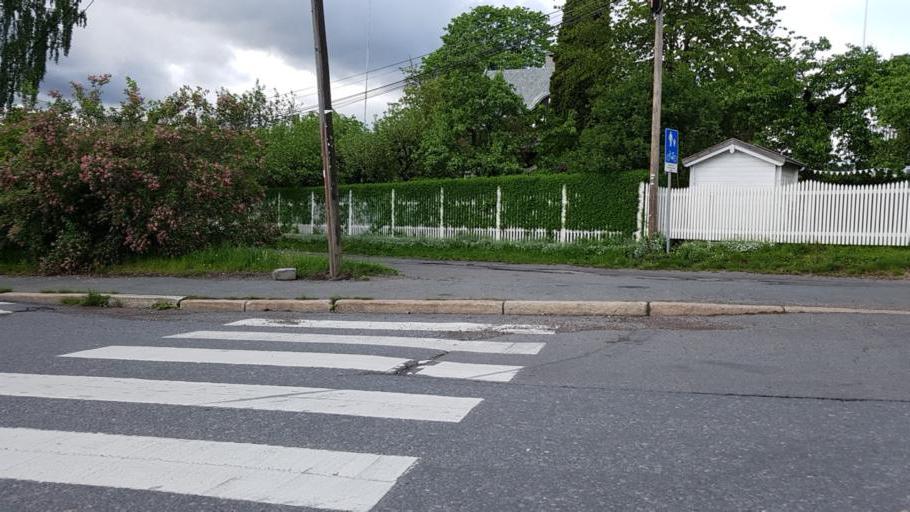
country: NO
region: Oslo
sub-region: Oslo
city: Oslo
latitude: 59.9436
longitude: 10.7879
